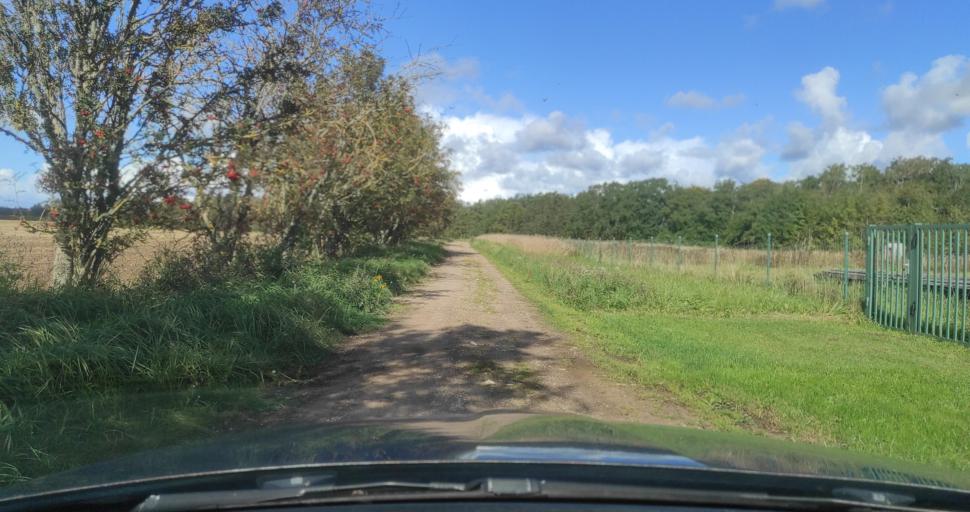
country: LV
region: Ventspils Rajons
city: Piltene
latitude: 57.2674
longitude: 21.6057
